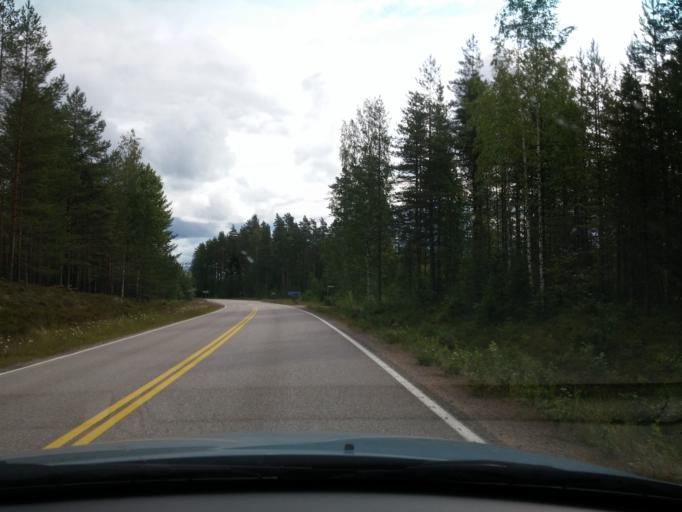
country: FI
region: Central Finland
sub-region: Saarijaervi-Viitasaari
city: Saarijaervi
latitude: 62.7982
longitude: 25.4269
